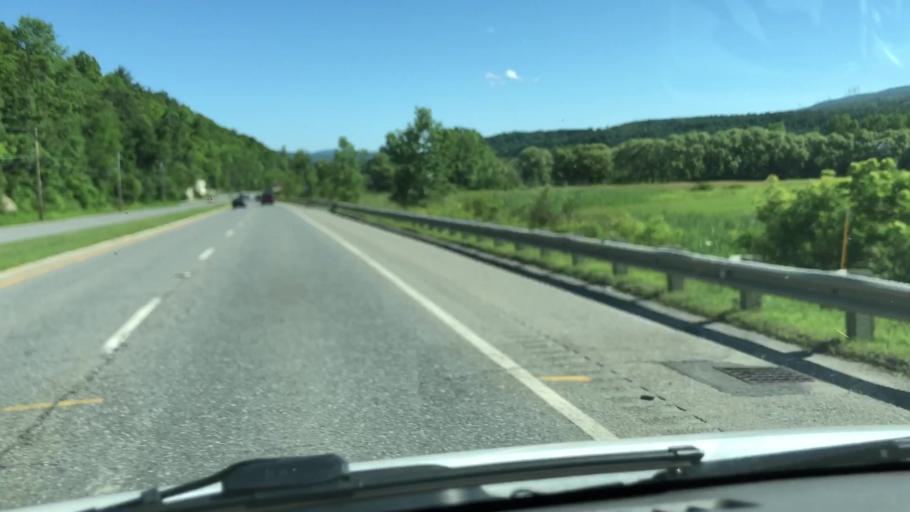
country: US
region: Massachusetts
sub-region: Berkshire County
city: North Adams
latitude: 42.6738
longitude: -73.1072
